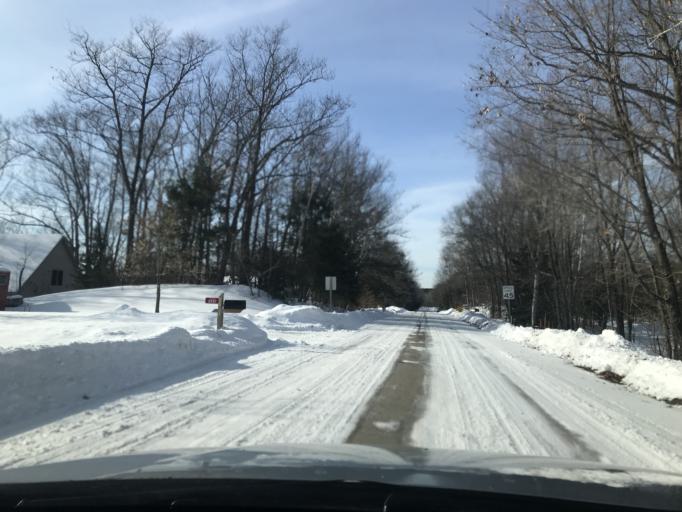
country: US
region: Wisconsin
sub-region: Oconto County
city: Gillett
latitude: 45.1571
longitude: -88.2014
